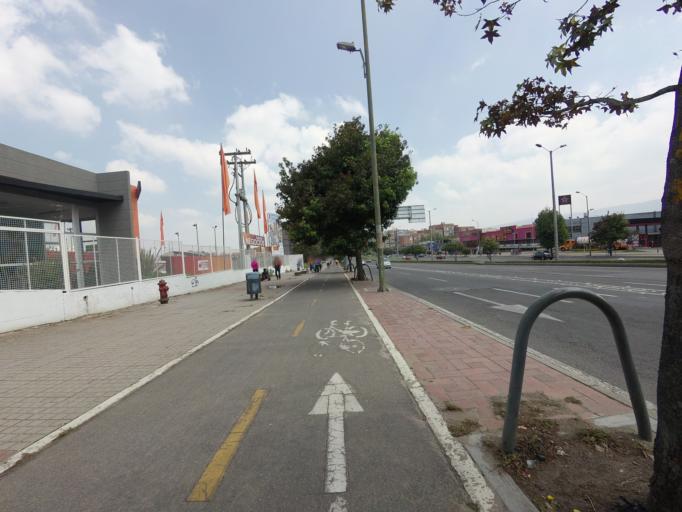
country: CO
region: Bogota D.C.
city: Barrio San Luis
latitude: 4.7240
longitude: -74.0732
